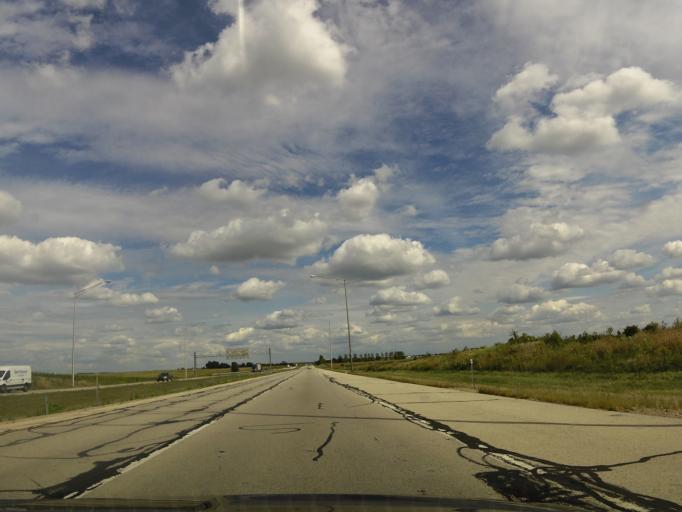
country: US
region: Illinois
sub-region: DeKalb County
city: Malta
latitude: 41.8997
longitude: -88.8632
